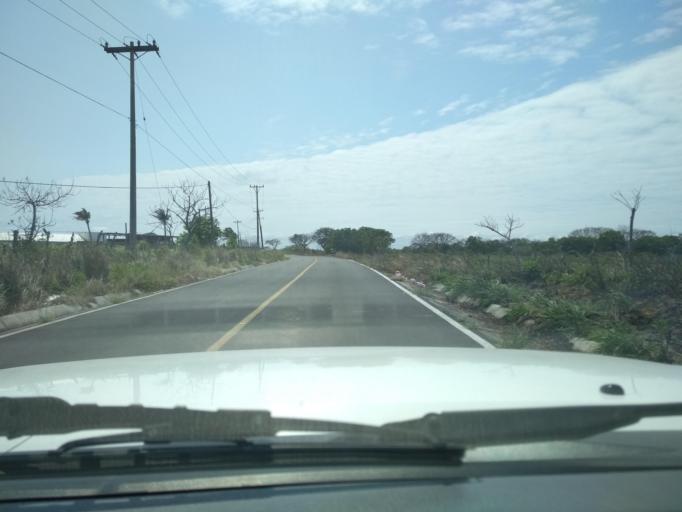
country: MX
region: Veracruz
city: Anton Lizardo
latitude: 19.0137
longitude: -95.9947
